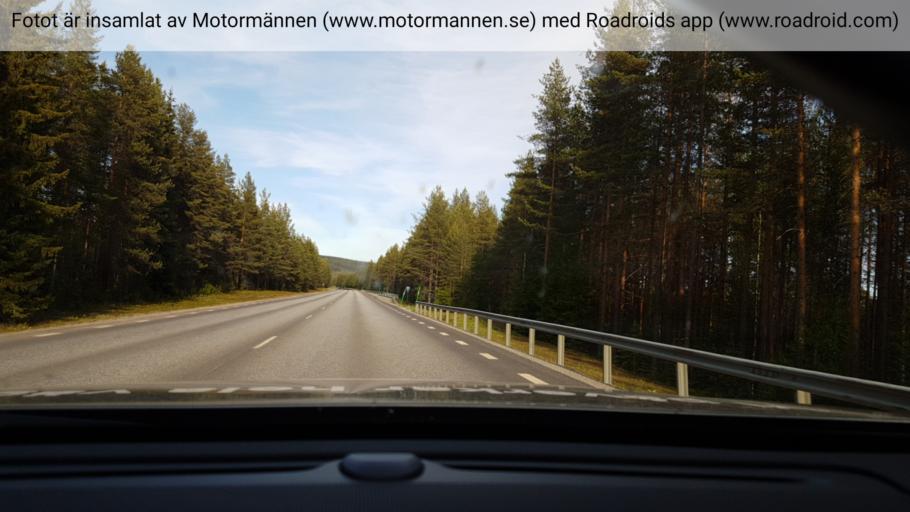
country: SE
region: Vaesterbotten
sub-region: Vindelns Kommun
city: Vindeln
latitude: 64.1432
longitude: 19.8873
